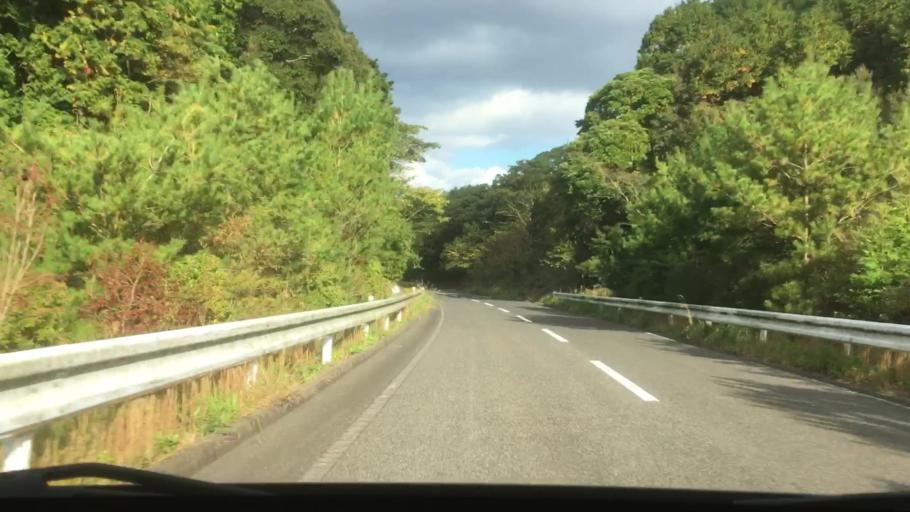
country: JP
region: Nagasaki
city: Sasebo
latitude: 33.0246
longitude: 129.6975
